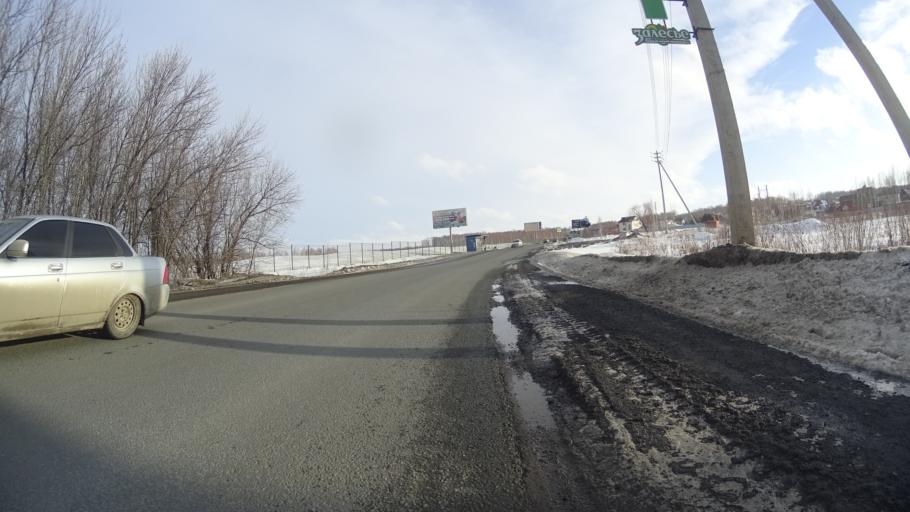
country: RU
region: Chelyabinsk
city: Sargazy
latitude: 55.1347
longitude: 61.2854
